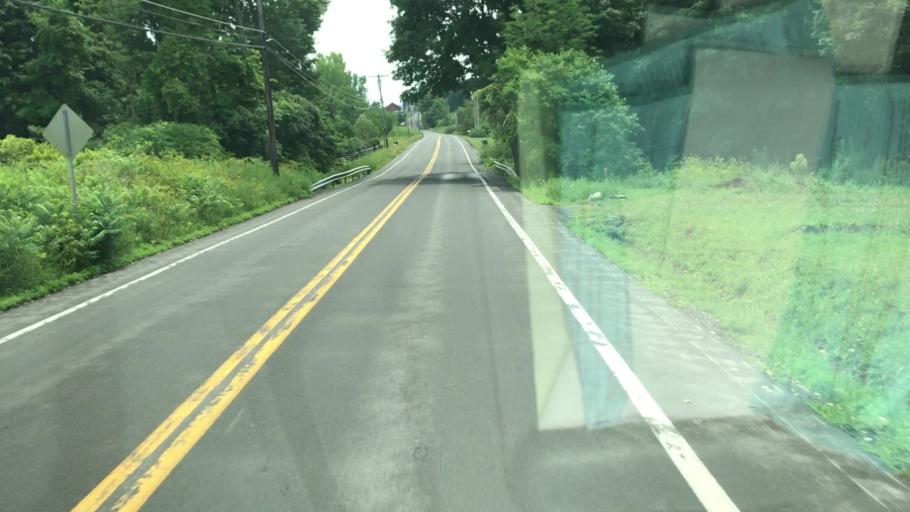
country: US
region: New York
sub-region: Onondaga County
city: Manlius
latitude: 42.9667
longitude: -75.9872
